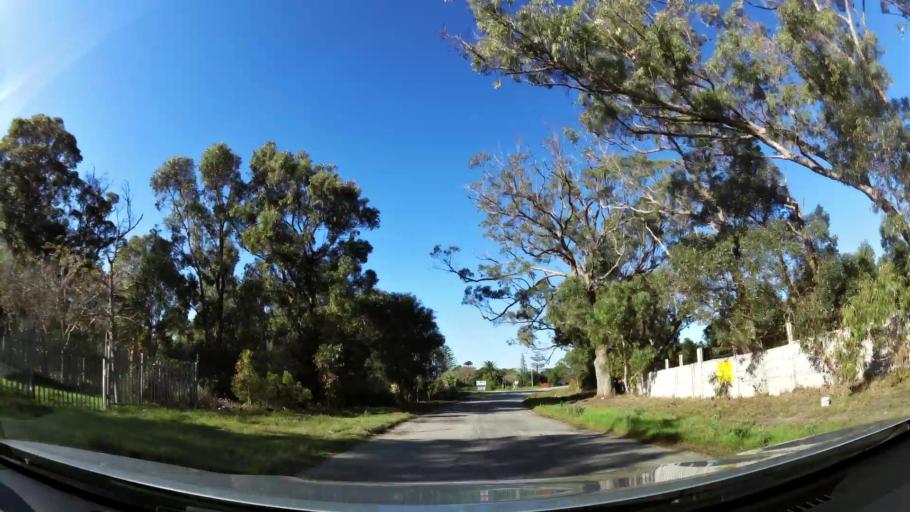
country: ZA
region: Eastern Cape
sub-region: Nelson Mandela Bay Metropolitan Municipality
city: Port Elizabeth
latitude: -33.9855
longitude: 25.6332
